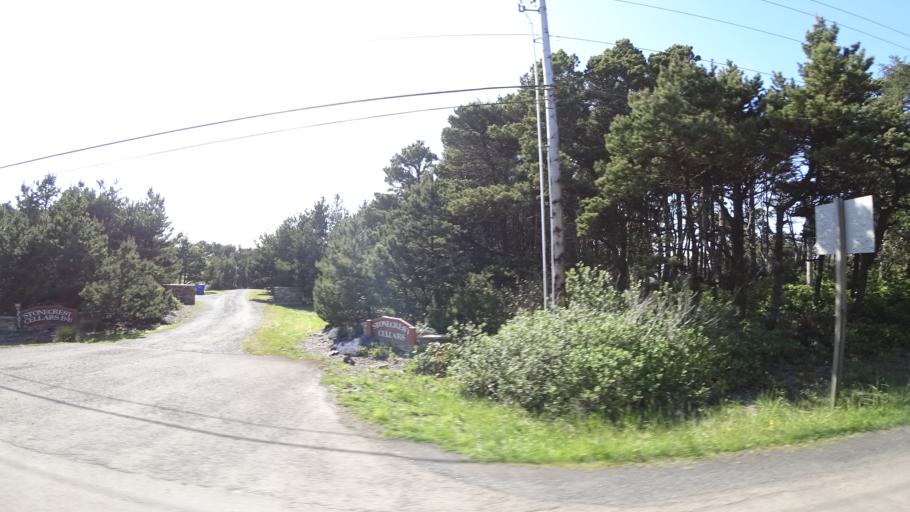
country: US
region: Oregon
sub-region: Lincoln County
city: Newport
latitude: 44.5696
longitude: -124.0681
